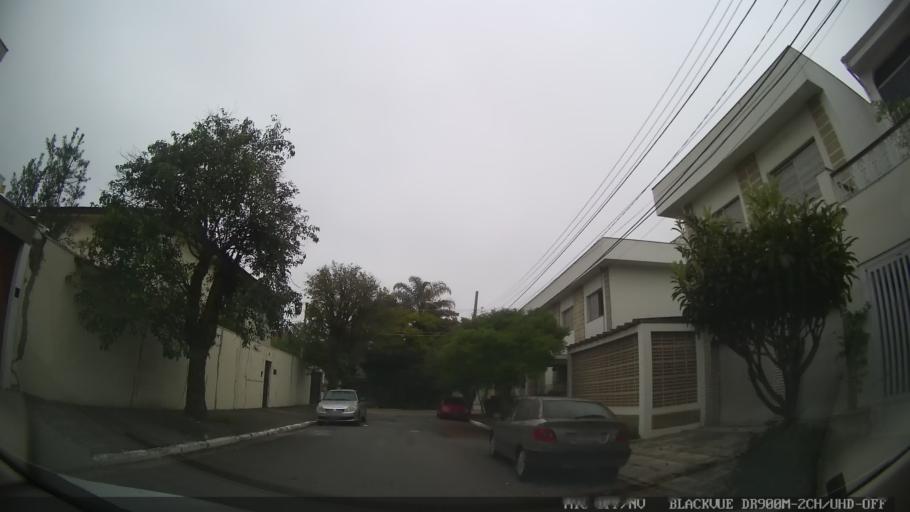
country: BR
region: Sao Paulo
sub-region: Sao Paulo
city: Sao Paulo
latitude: -23.5835
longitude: -46.6207
